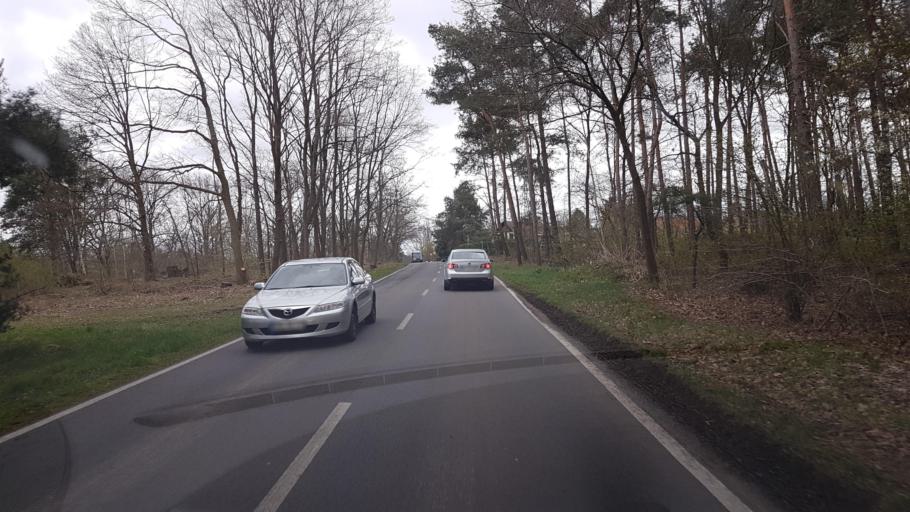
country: DE
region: Saxony
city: Wittichenau
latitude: 51.3819
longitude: 14.2664
